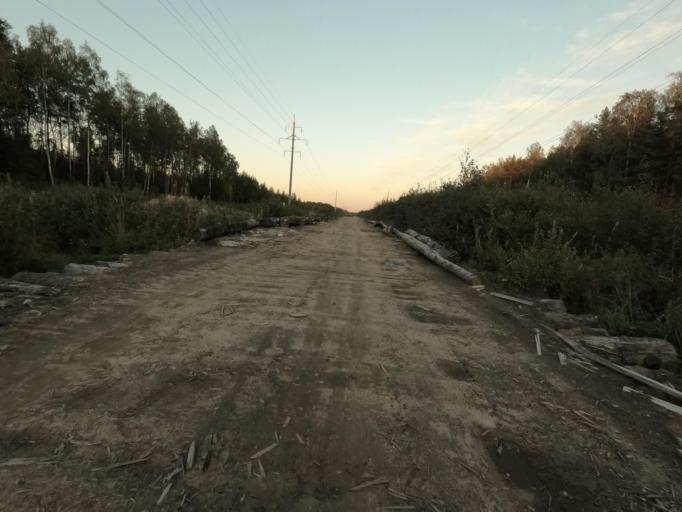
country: RU
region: Leningrad
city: Otradnoye
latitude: 59.7659
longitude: 30.8216
